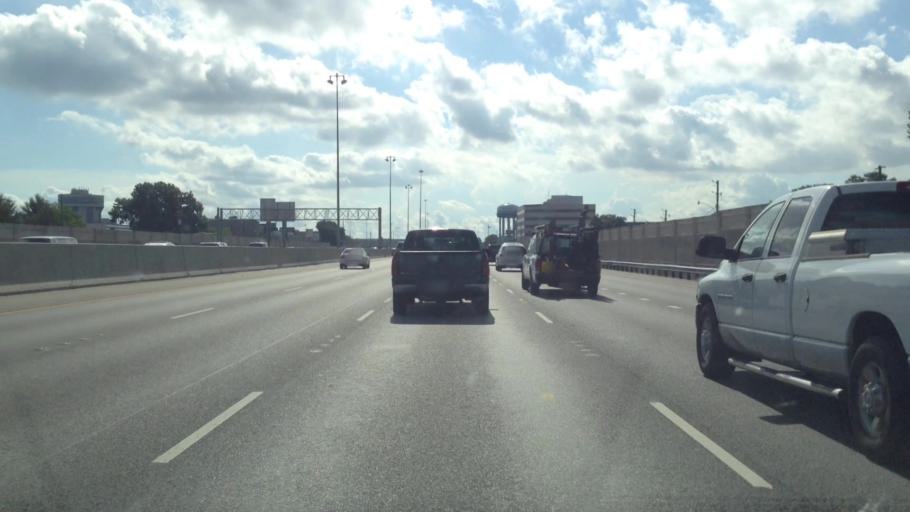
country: US
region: Louisiana
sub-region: Jefferson Parish
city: Metairie Terrace
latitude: 29.9979
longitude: -90.1677
